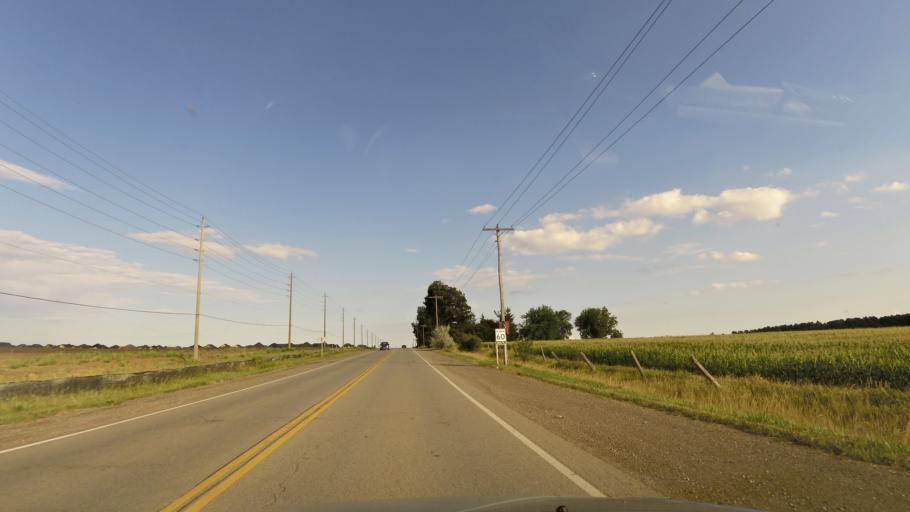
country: CA
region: Ontario
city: Brampton
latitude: 43.6865
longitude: -79.8562
